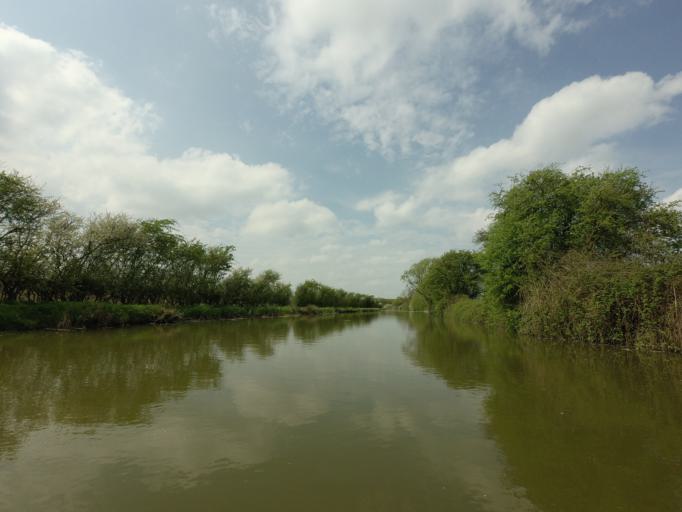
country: GB
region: England
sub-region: Central Bedfordshire
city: Leighton Buzzard
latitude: 51.8859
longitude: -0.6579
